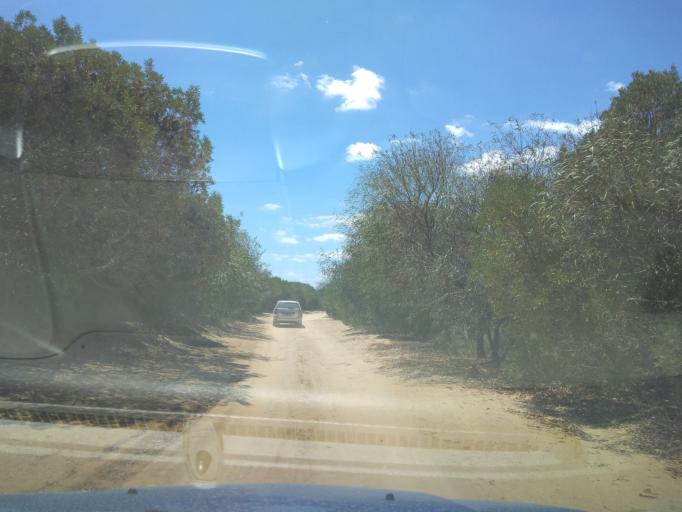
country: TN
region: Susah
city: Harqalah
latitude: 36.1612
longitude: 10.4639
